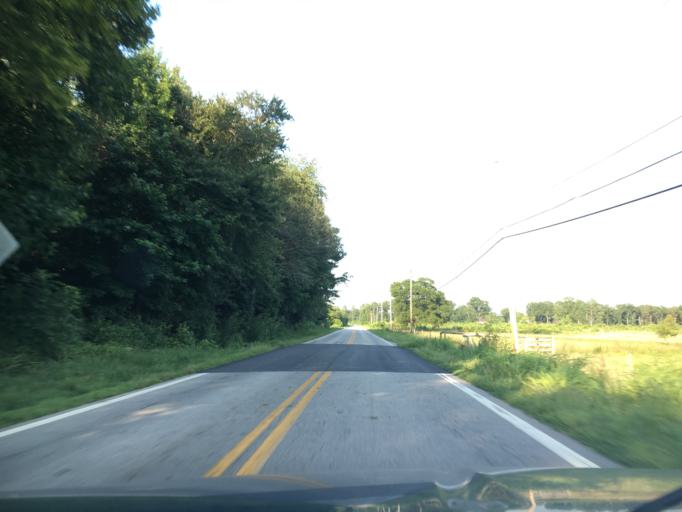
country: US
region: Virginia
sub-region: Pittsylvania County
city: Chatham
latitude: 36.8166
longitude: -79.3434
